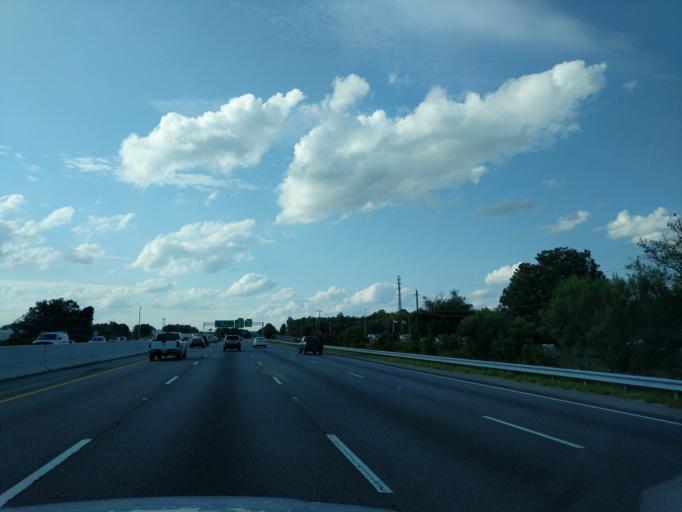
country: US
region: South Carolina
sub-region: Greenville County
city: Simpsonville
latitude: 34.7469
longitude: -82.2803
